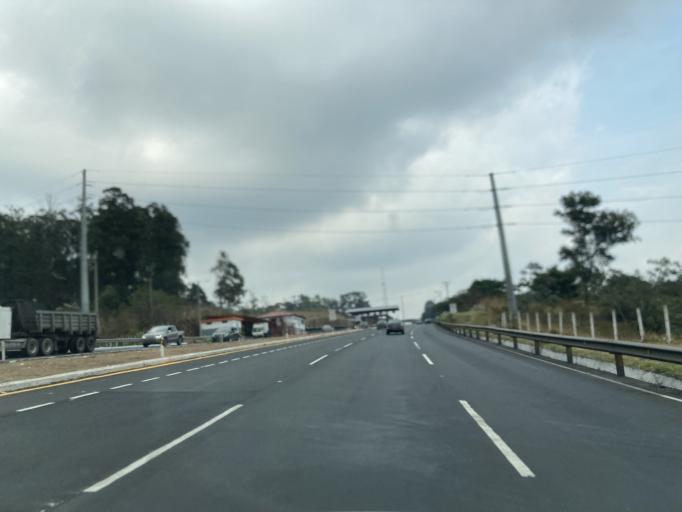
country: GT
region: Escuintla
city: Palin
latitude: 14.4071
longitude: -90.7044
